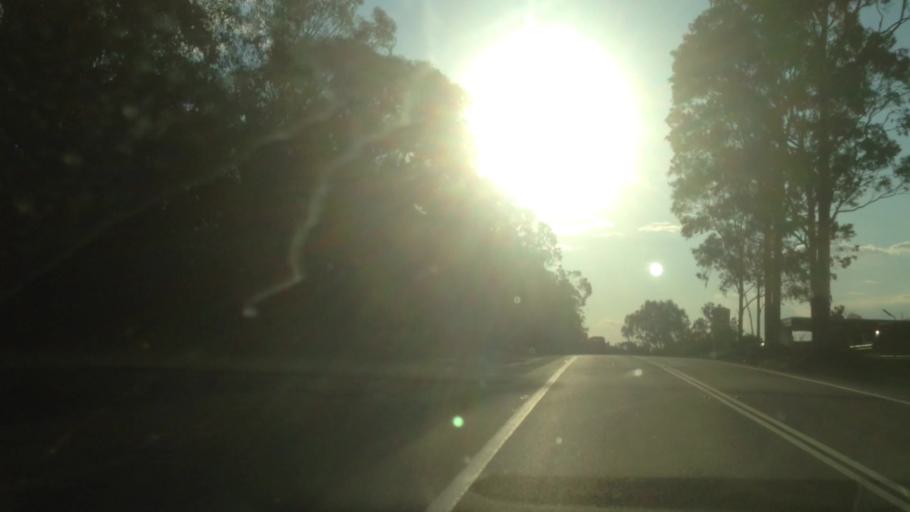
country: AU
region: New South Wales
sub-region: Cessnock
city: Kurri Kurri
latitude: -32.8282
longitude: 151.4925
